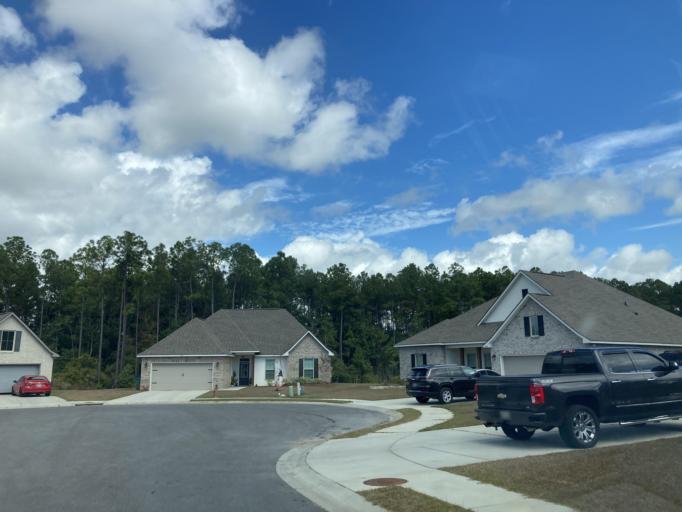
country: US
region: Mississippi
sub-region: Jackson County
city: Gulf Hills
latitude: 30.4526
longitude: -88.8286
